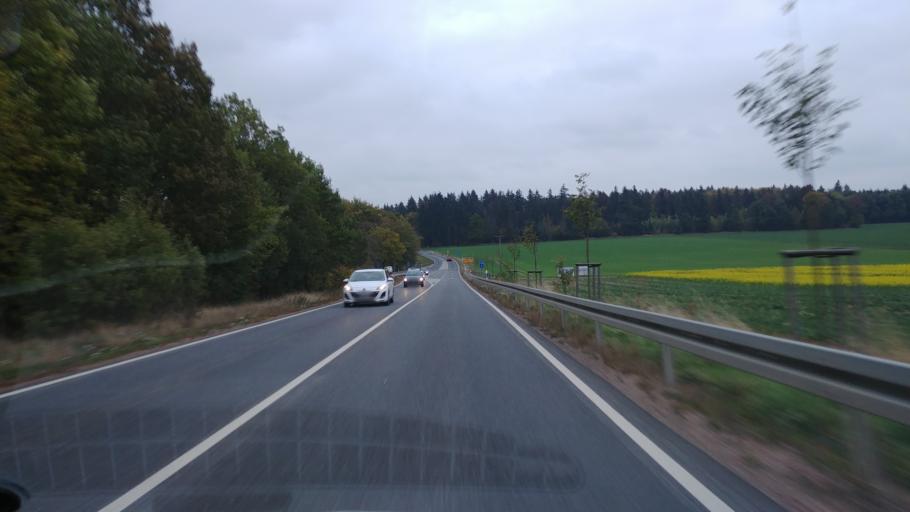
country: DE
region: Rheinland-Pfalz
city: Kaltenholzhausen
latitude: 50.2675
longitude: 8.1717
